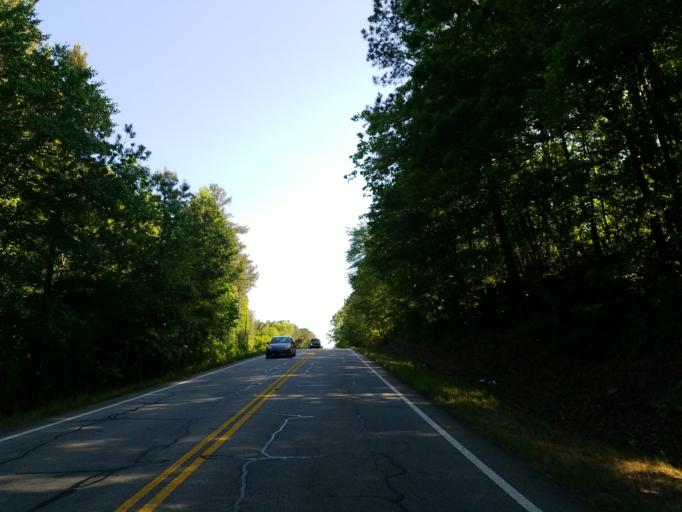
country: US
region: Georgia
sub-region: Paulding County
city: Dallas
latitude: 33.8834
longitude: -84.8837
